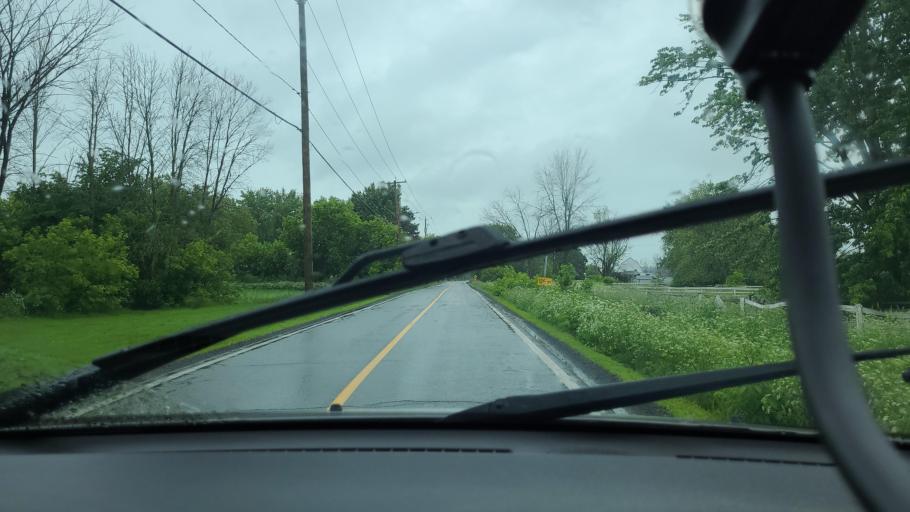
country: CA
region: Quebec
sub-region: Monteregie
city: Saint-Basile-le-Grand
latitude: 45.5478
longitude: -73.2708
